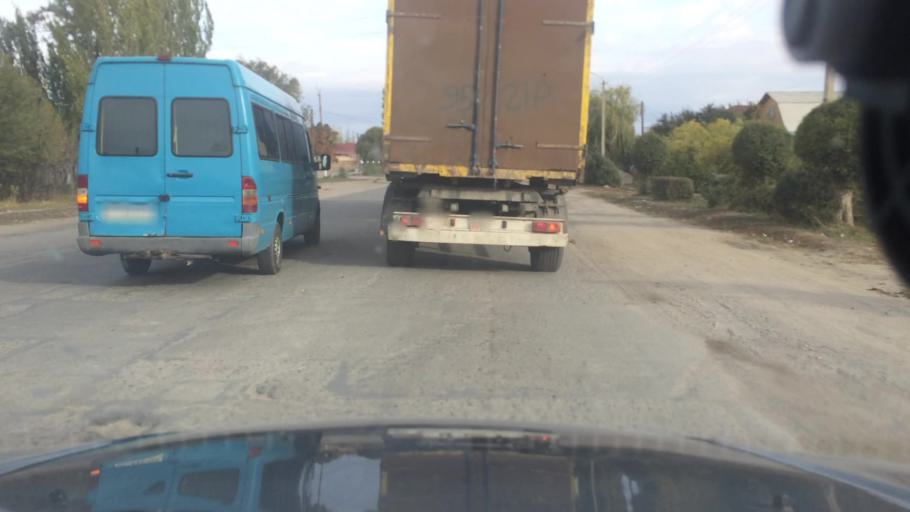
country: KG
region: Ysyk-Koel
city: Karakol
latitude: 42.5169
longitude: 78.3858
